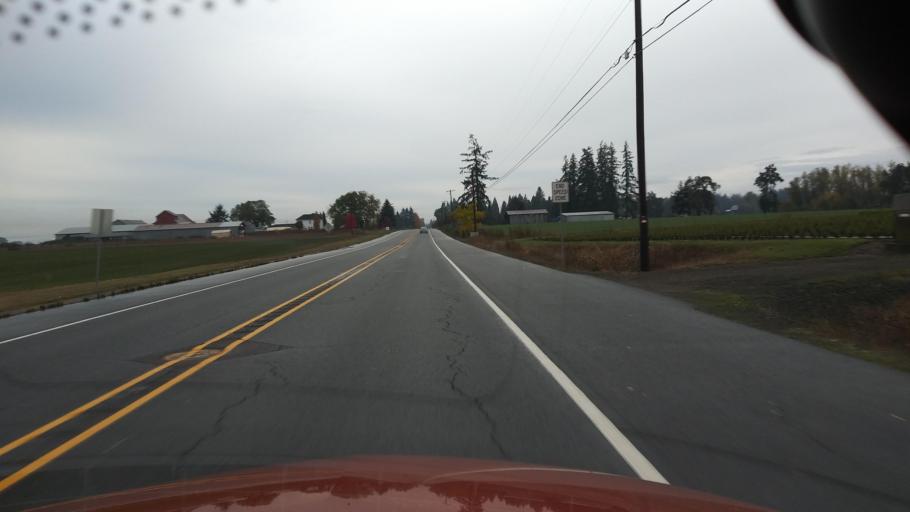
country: US
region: Oregon
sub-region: Washington County
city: Cornelius
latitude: 45.5330
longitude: -123.0597
